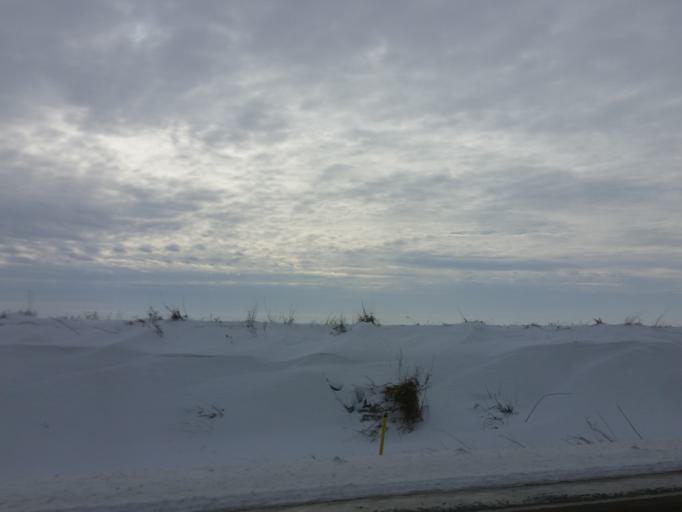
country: US
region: Iowa
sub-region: Dubuque County
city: Peosta
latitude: 42.3821
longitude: -90.7488
